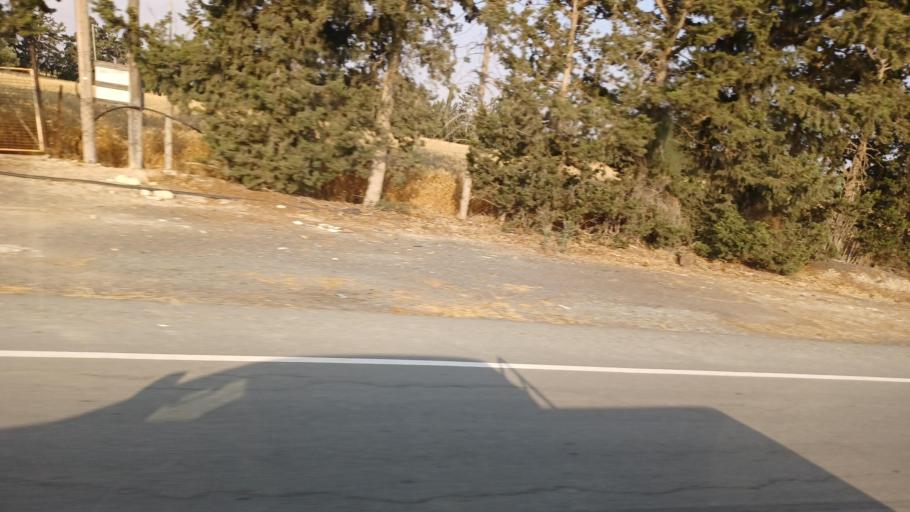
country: CY
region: Larnaka
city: Tersefanou
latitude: 34.8251
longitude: 33.5136
